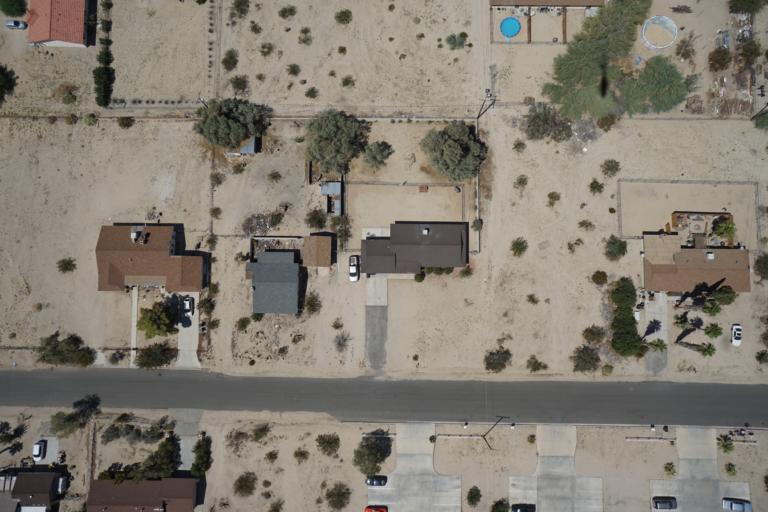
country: US
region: California
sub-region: San Bernardino County
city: Twentynine Palms
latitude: 34.1335
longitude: -116.0525
